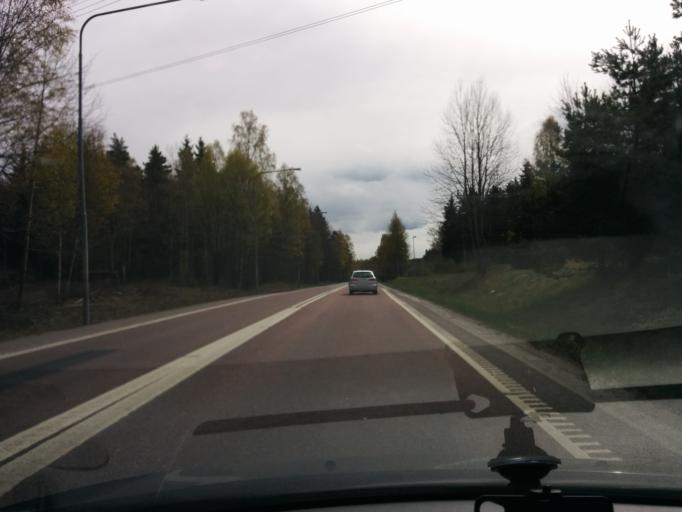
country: SE
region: Stockholm
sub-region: Botkyrka Kommun
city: Fittja
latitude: 59.2436
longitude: 17.8919
